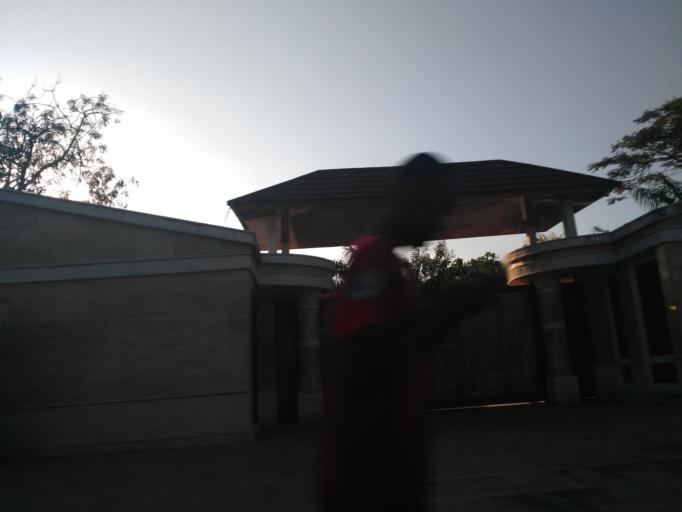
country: TZ
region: Dar es Salaam
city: Magomeni
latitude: -6.7621
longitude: 39.2807
